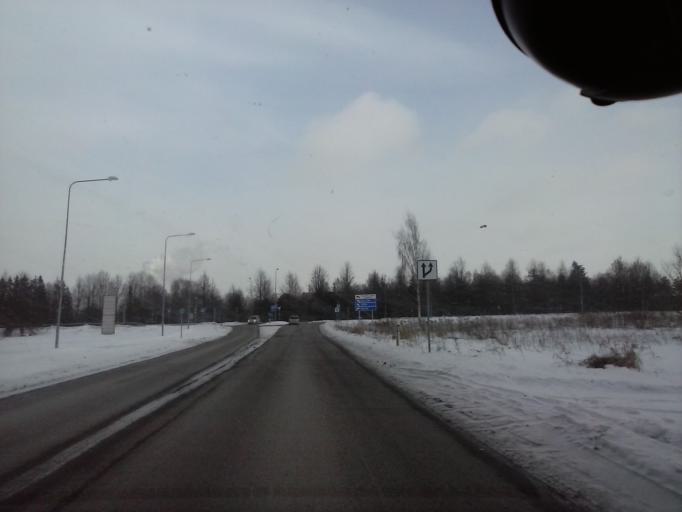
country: EE
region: Tartu
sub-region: Tartu linn
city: Tartu
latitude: 58.3549
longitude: 26.6760
